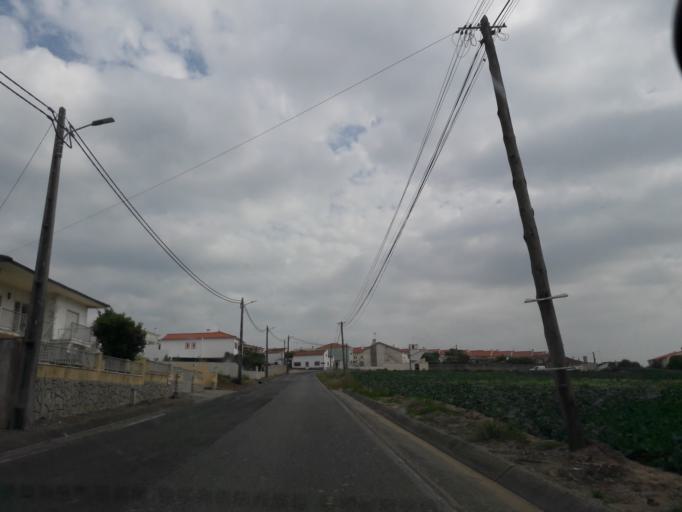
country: PT
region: Leiria
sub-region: Peniche
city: Atouguia da Baleia
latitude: 39.3524
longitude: -9.2928
